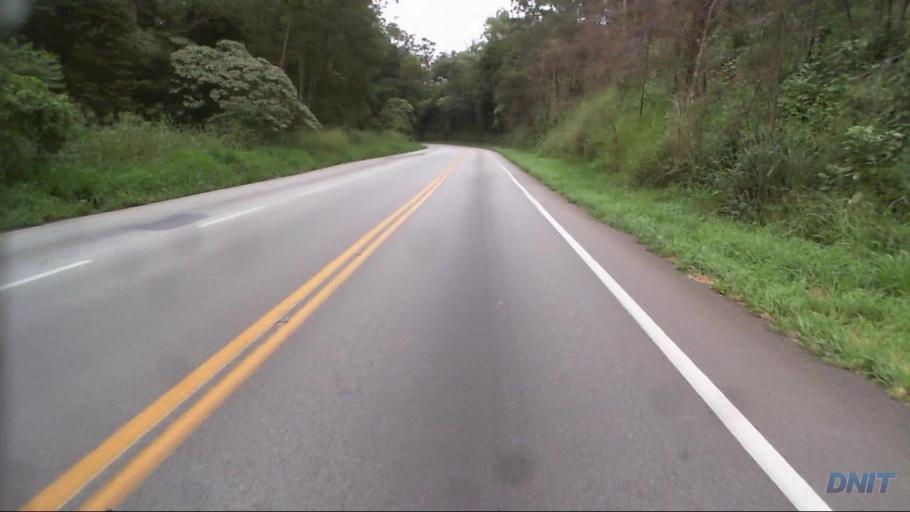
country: BR
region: Minas Gerais
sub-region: Joao Monlevade
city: Joao Monlevade
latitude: -19.8459
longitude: -43.1079
